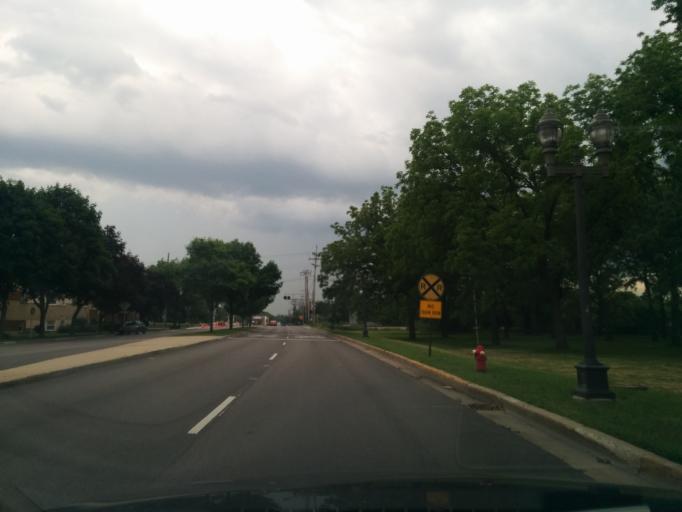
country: US
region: Illinois
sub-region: Cook County
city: North Riverside
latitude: 41.8494
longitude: -87.8233
